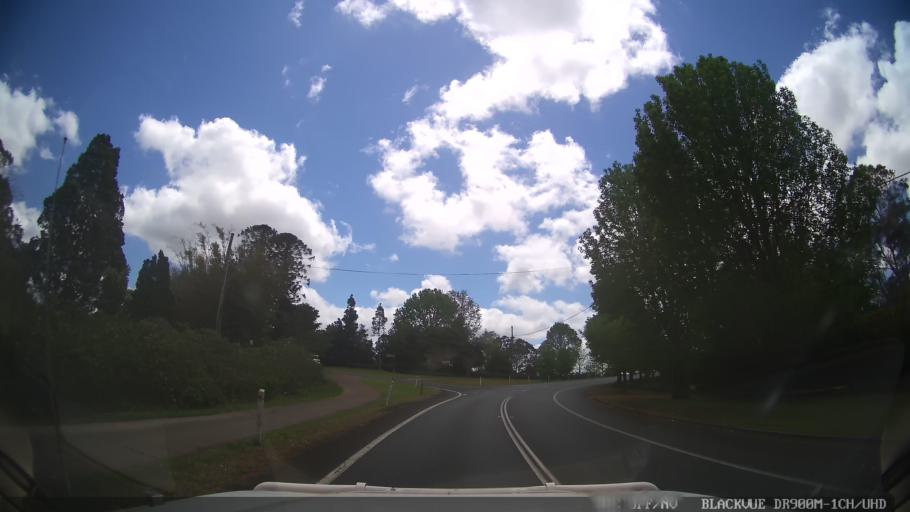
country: AU
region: Queensland
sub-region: Sunshine Coast
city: Nambour
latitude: -26.6648
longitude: 152.8799
